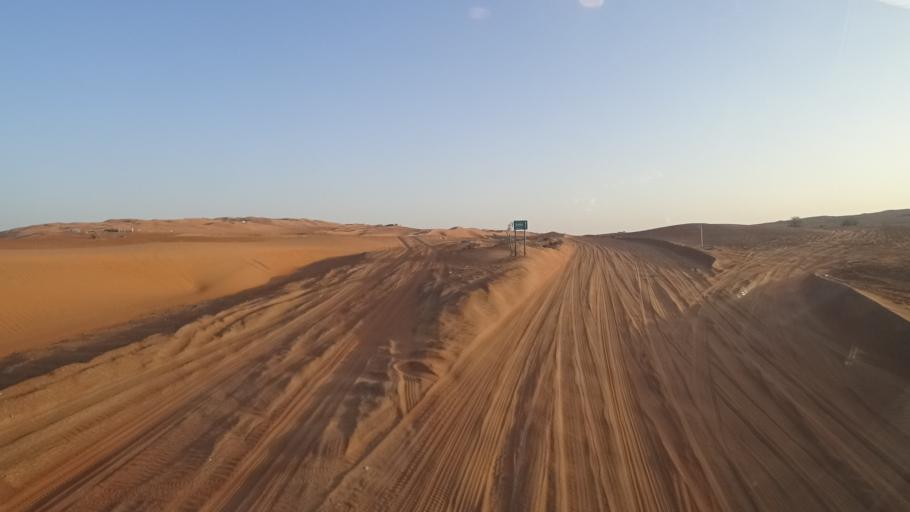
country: OM
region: Ash Sharqiyah
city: Badiyah
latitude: 22.4892
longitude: 58.7295
